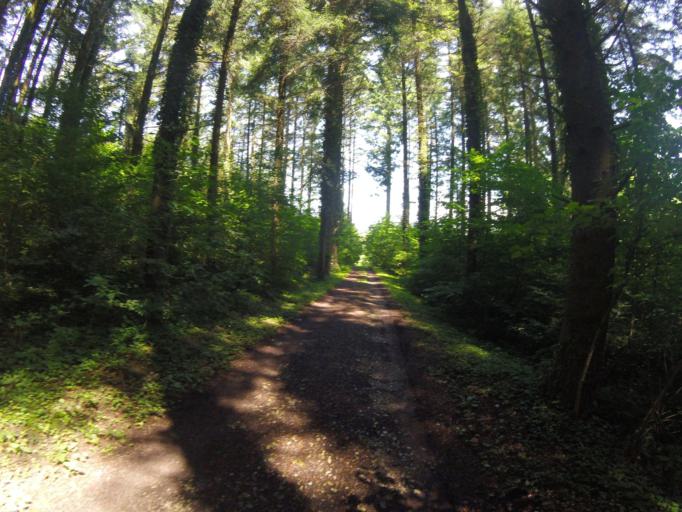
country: HU
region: Zala
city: Letenye
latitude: 46.5074
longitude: 16.6968
